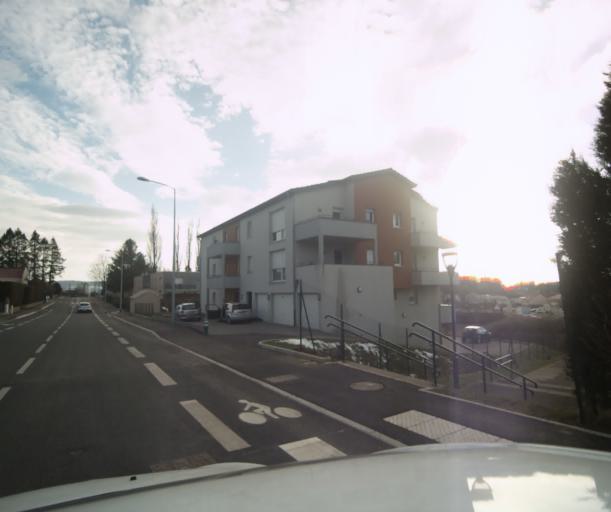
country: FR
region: Franche-Comte
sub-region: Departement du Doubs
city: Besancon
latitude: 47.2648
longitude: 6.0274
